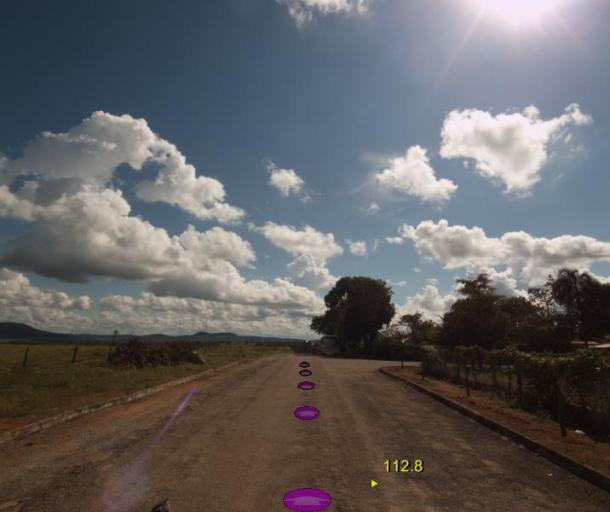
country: BR
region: Goias
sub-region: Pirenopolis
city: Pirenopolis
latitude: -15.8287
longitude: -49.1355
